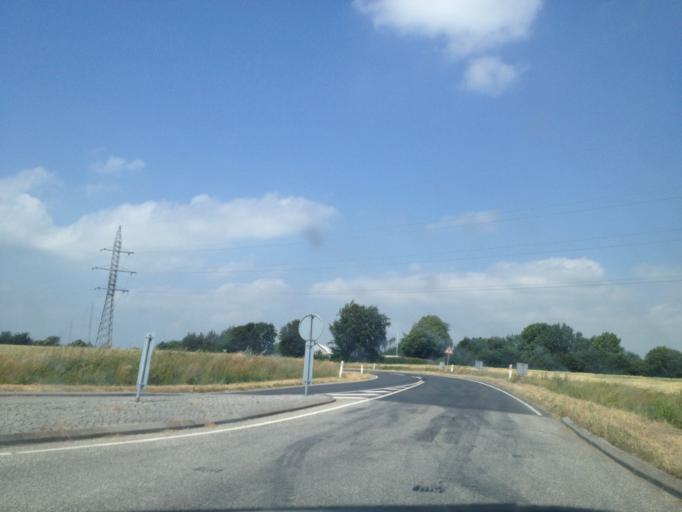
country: DK
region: South Denmark
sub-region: Haderslev Kommune
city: Vojens
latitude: 55.3353
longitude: 9.2989
